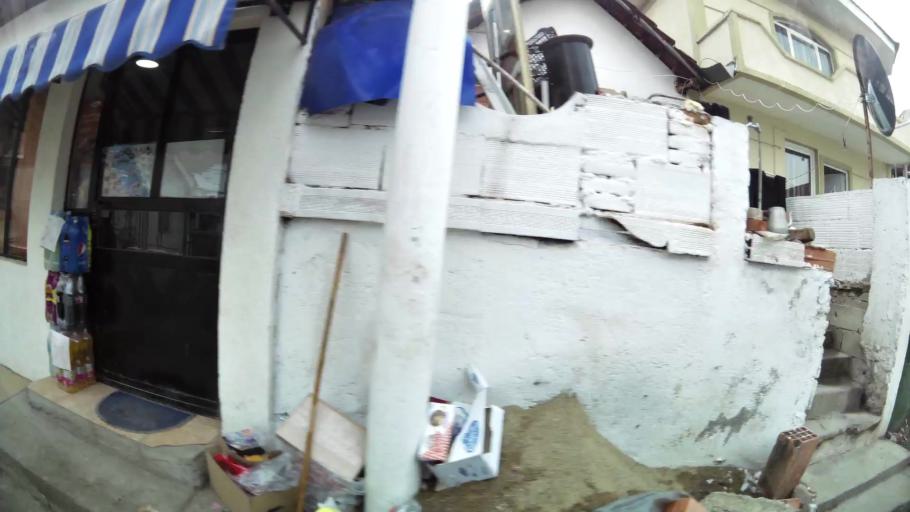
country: MK
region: Suto Orizari
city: Suto Orizare
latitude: 42.0367
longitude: 21.4224
